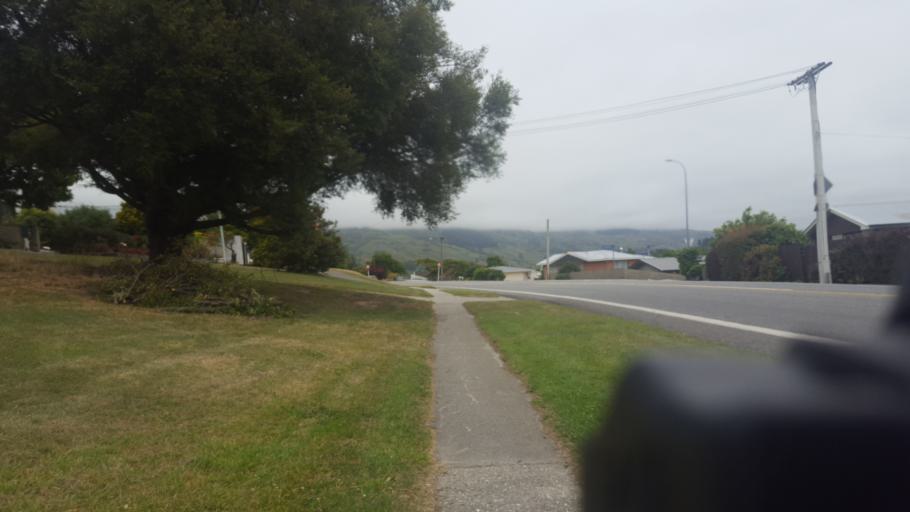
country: NZ
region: Otago
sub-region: Queenstown-Lakes District
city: Kingston
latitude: -45.5375
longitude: 169.3099
